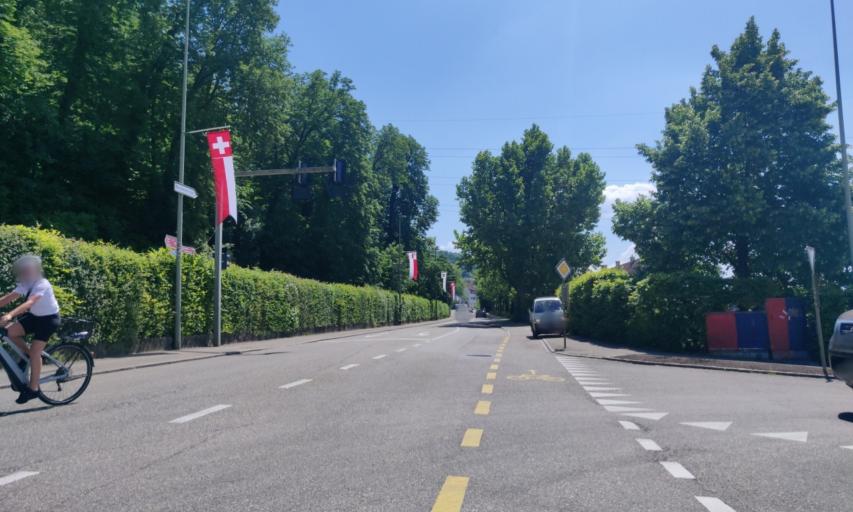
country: CH
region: Basel-Landschaft
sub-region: Bezirk Arlesheim
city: Munchenstein
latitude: 47.5167
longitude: 7.6192
